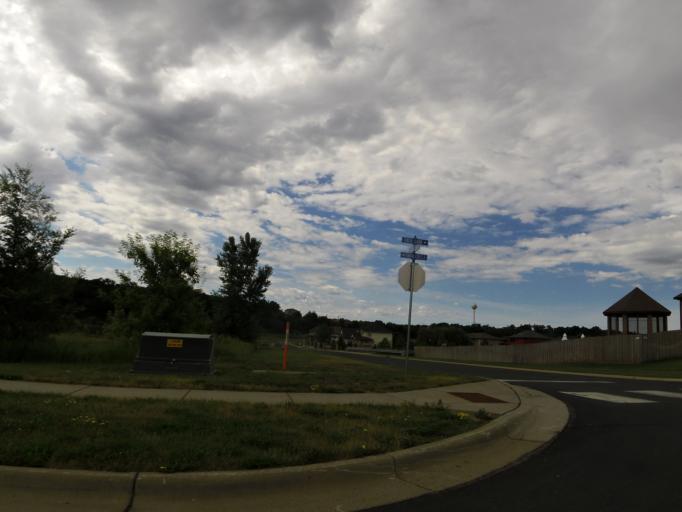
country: US
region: Minnesota
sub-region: Scott County
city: Prior Lake
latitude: 44.7606
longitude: -93.4444
